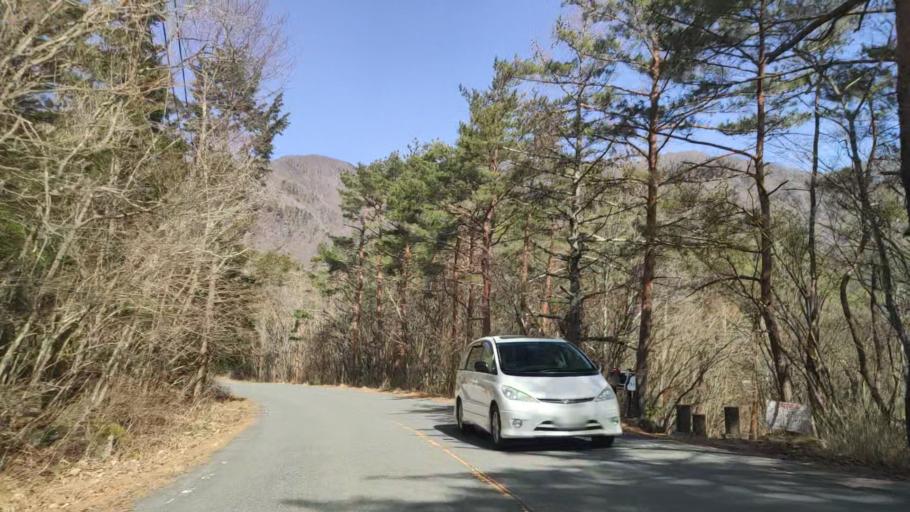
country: JP
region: Yamanashi
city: Fujikawaguchiko
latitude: 35.4976
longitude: 138.6644
